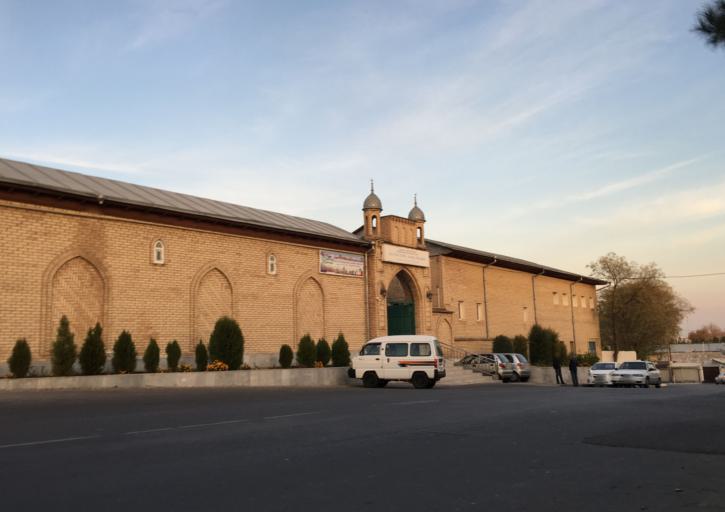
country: UZ
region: Toshkent
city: Salor
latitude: 41.3274
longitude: 69.3512
